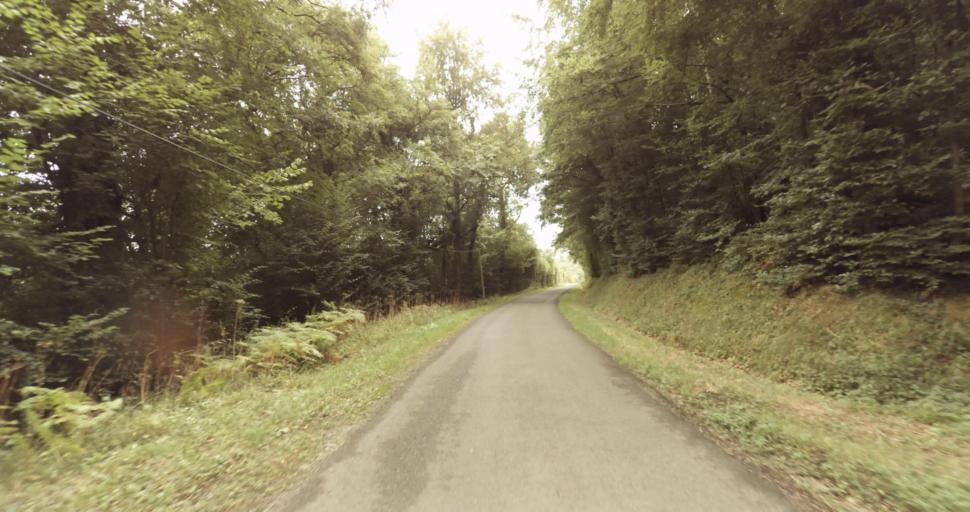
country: FR
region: Lower Normandy
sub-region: Departement de l'Orne
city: Vimoutiers
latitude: 48.9308
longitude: 0.3120
